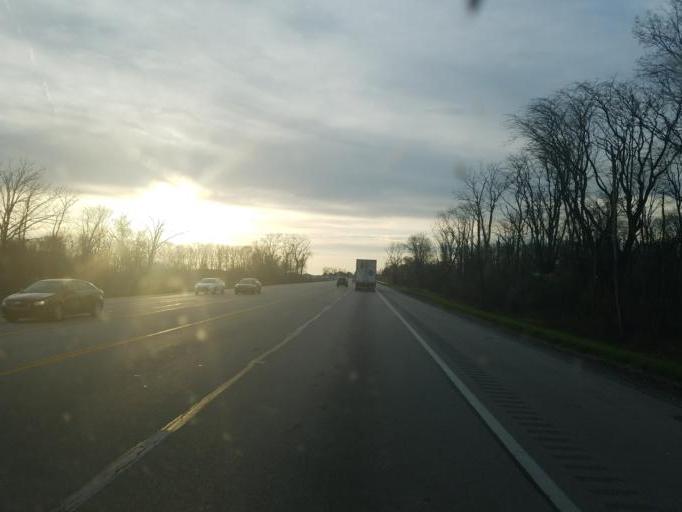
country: US
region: Ohio
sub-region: Sandusky County
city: Woodville
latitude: 41.4733
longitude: -83.4185
